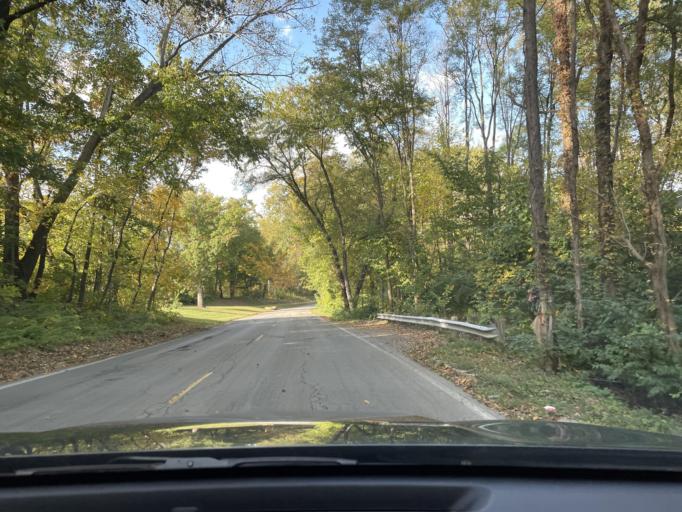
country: US
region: Missouri
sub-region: Buchanan County
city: Saint Joseph
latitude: 39.7324
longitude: -94.8386
